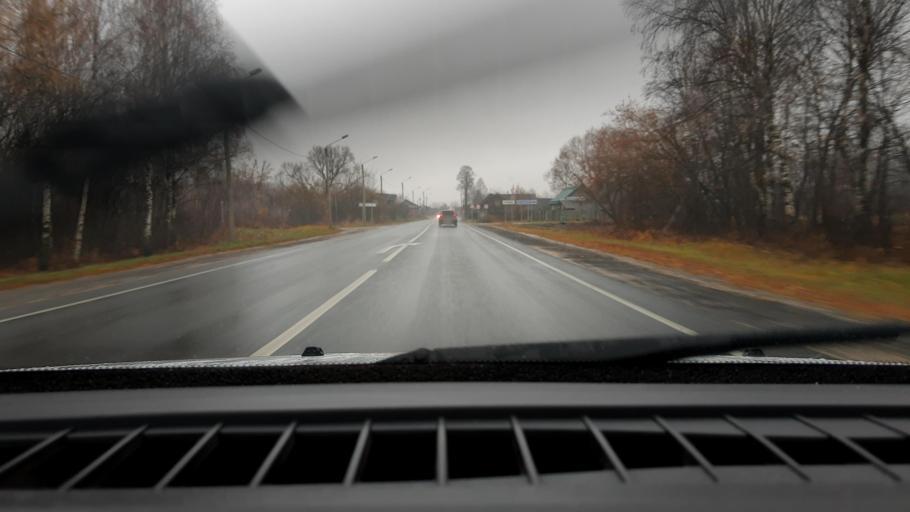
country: RU
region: Nizjnij Novgorod
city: Linda
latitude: 56.5474
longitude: 44.0200
